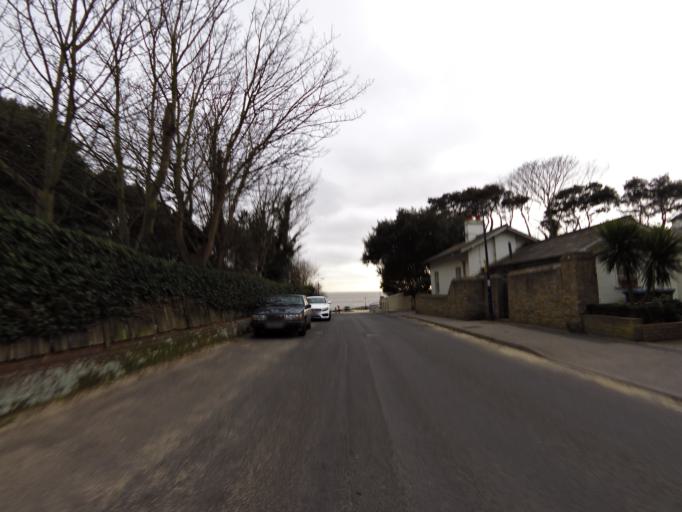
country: GB
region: England
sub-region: Suffolk
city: Felixstowe
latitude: 51.9644
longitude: 1.3678
